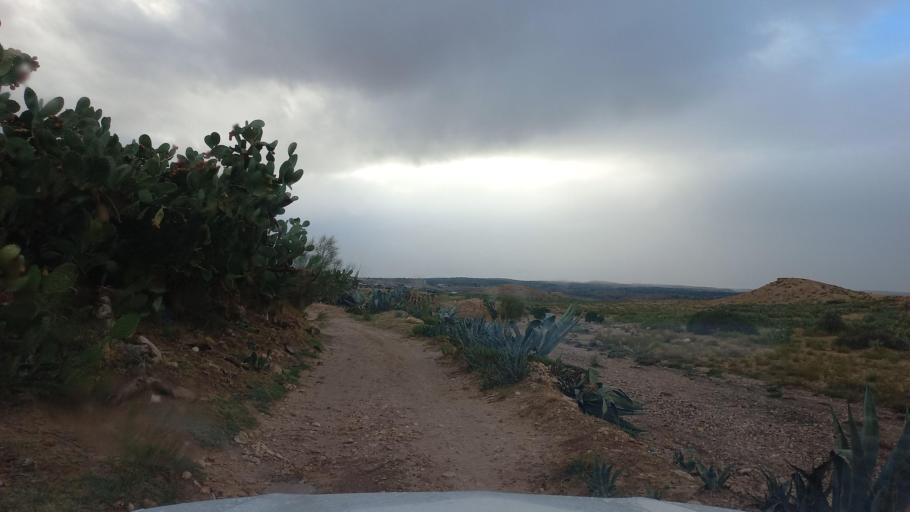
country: TN
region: Al Qasrayn
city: Kasserine
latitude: 35.2719
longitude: 8.9379
